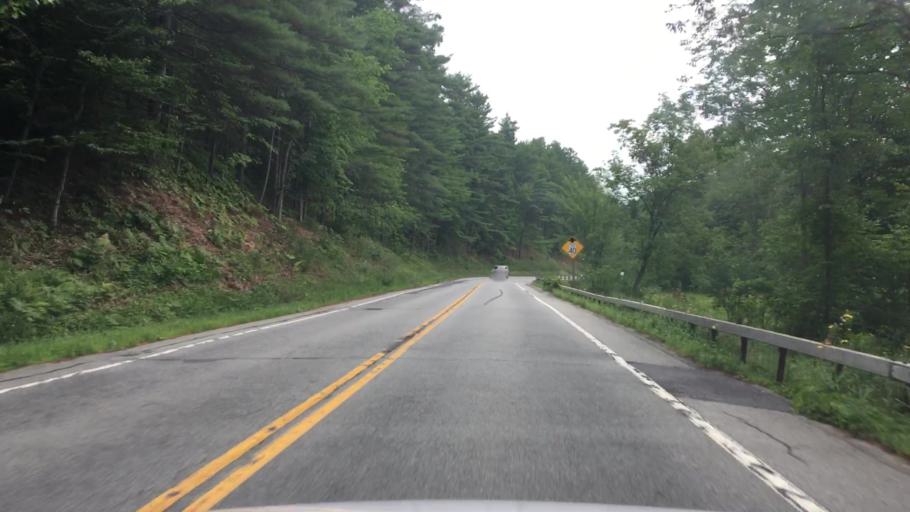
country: US
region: New York
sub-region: Essex County
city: Keeseville
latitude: 44.4265
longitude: -73.6800
